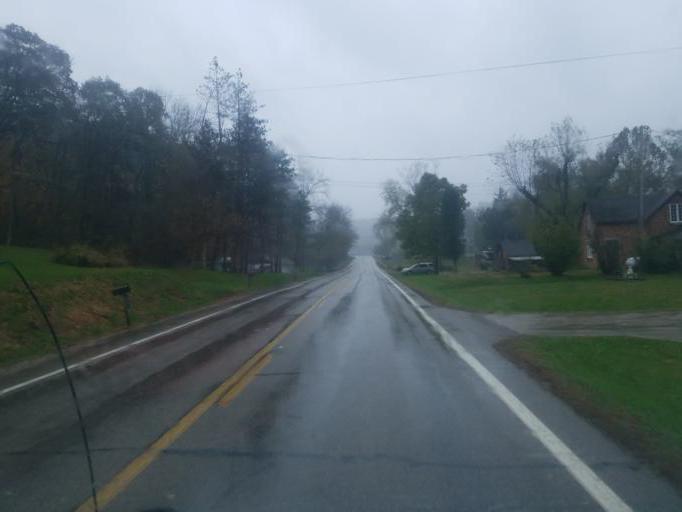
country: US
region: Ohio
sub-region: Morgan County
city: McConnelsville
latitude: 39.6851
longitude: -81.8865
